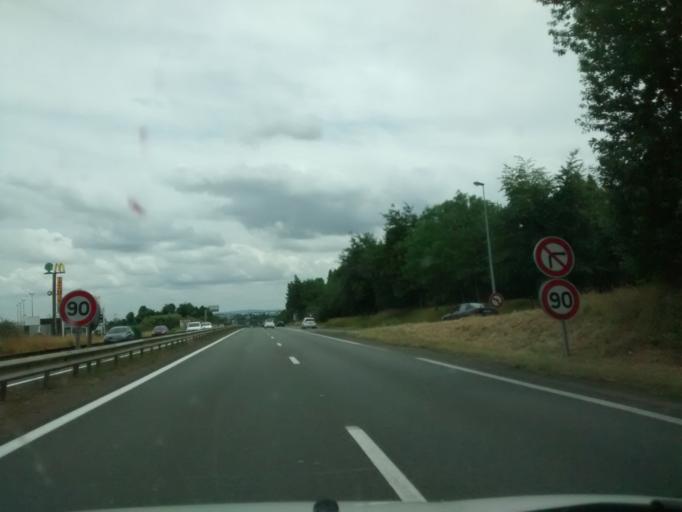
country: FR
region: Brittany
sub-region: Departement des Cotes-d'Armor
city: Saint-Brieuc
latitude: 48.5334
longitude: -2.7581
